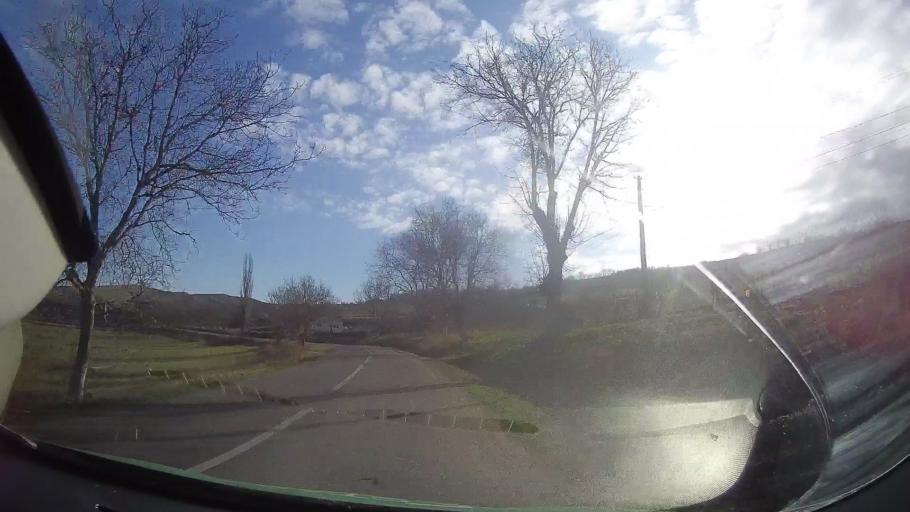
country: RO
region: Mures
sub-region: Comuna Iclanzel
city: Iclanzel
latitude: 46.5265
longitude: 24.2810
